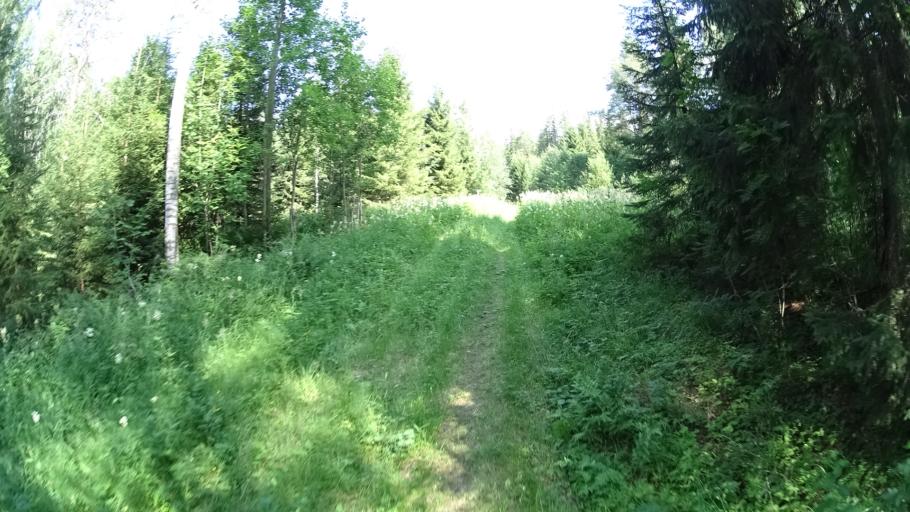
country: FI
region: North Karelia
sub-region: Pielisen Karjala
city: Lieksa
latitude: 63.1215
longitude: 29.8047
